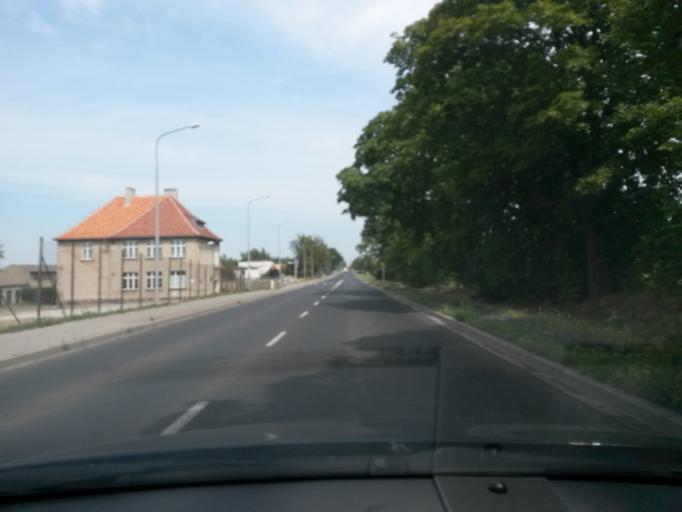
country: PL
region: Greater Poland Voivodeship
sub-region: Powiat sremski
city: Dolsk
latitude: 51.9535
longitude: 17.0660
